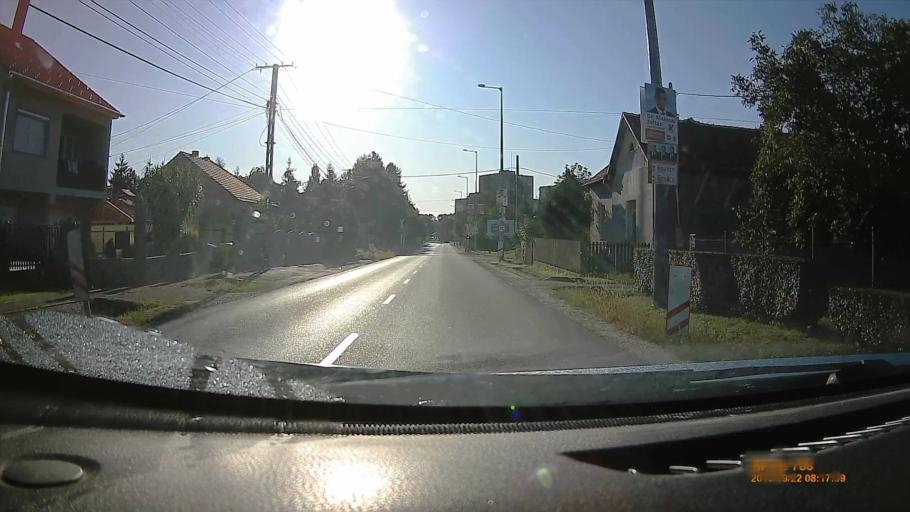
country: HU
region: Borsod-Abauj-Zemplen
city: Sajobabony
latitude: 48.1106
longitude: 20.6719
